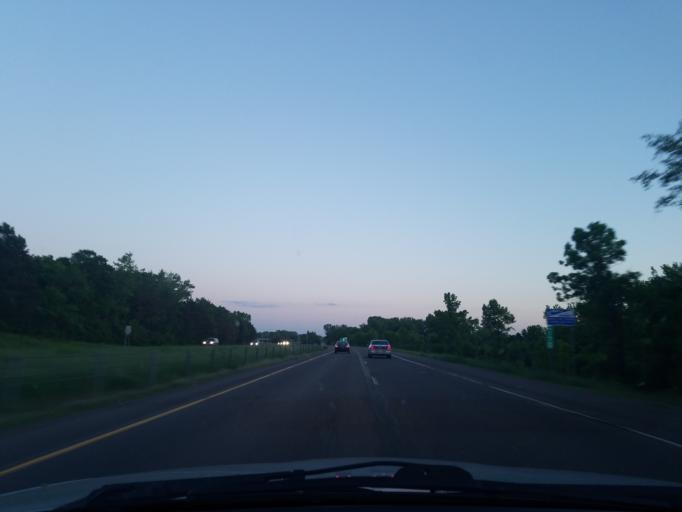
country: US
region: Minnesota
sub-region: Pine County
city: Pine City
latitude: 45.8289
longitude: -92.9836
